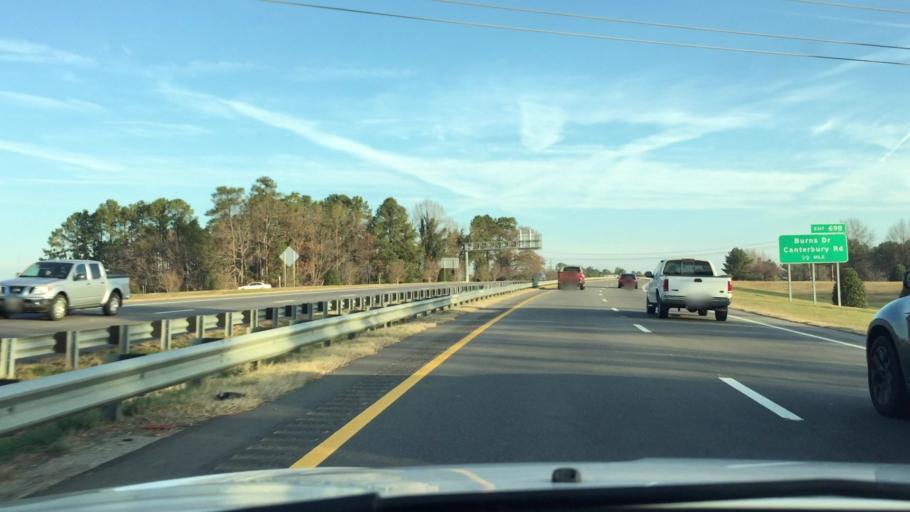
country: US
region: North Carolina
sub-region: Lee County
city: Sanford
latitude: 35.4927
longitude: -79.1963
